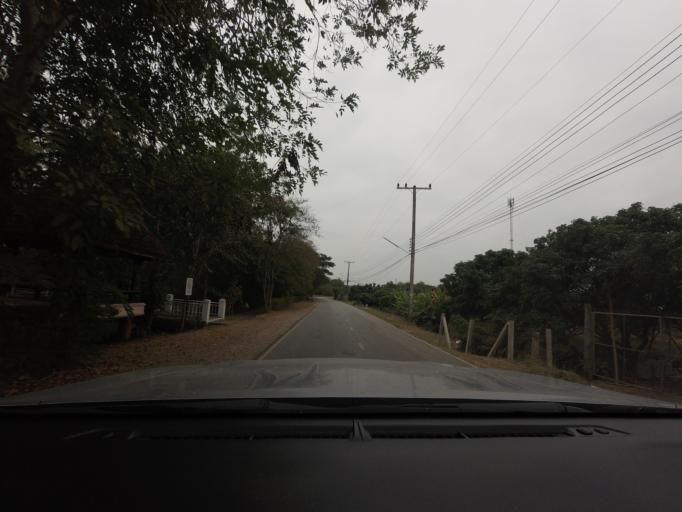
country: TH
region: Lamphun
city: Lamphun
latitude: 18.6161
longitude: 99.0225
